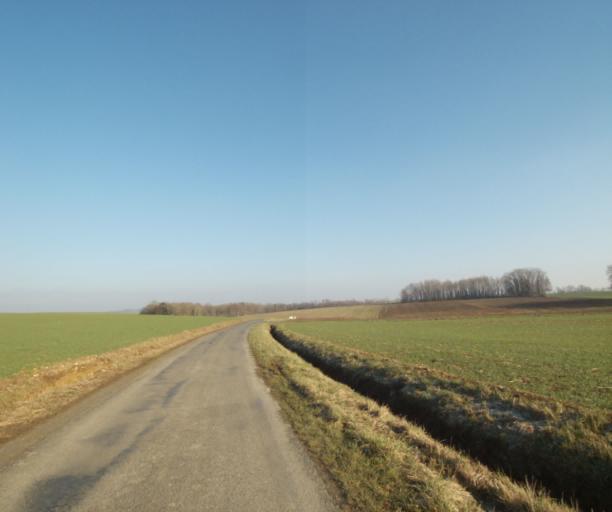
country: FR
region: Champagne-Ardenne
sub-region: Departement de la Haute-Marne
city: Bienville
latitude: 48.5479
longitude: 5.0366
